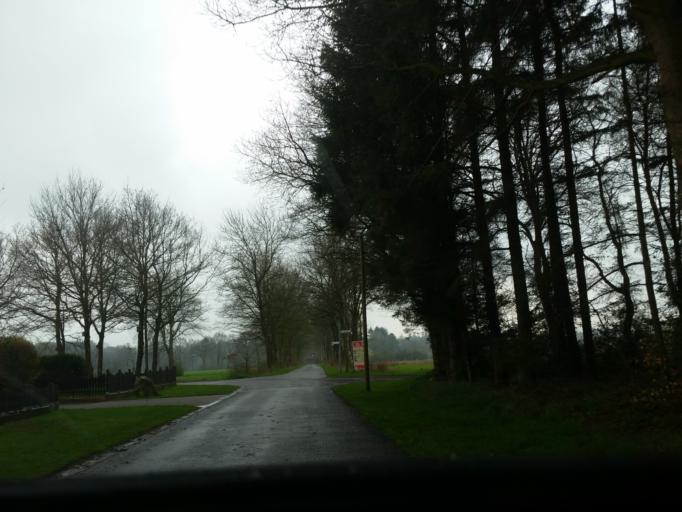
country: DE
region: Lower Saxony
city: Hipstedt
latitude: 53.4776
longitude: 8.9677
